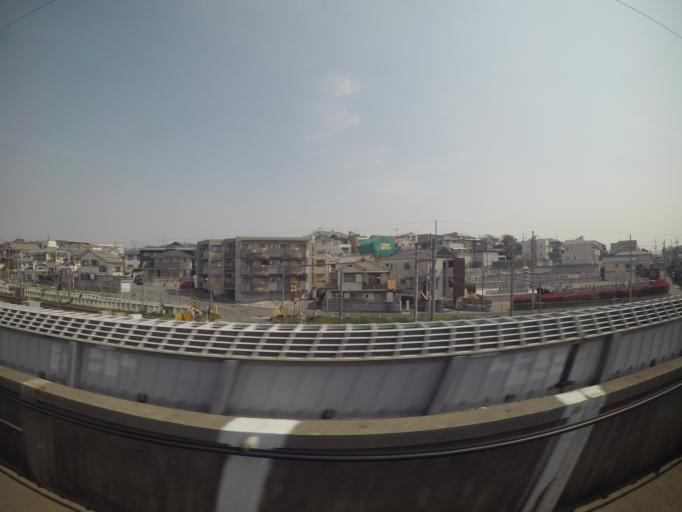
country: JP
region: Hyogo
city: Akashi
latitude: 34.6936
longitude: 134.9085
